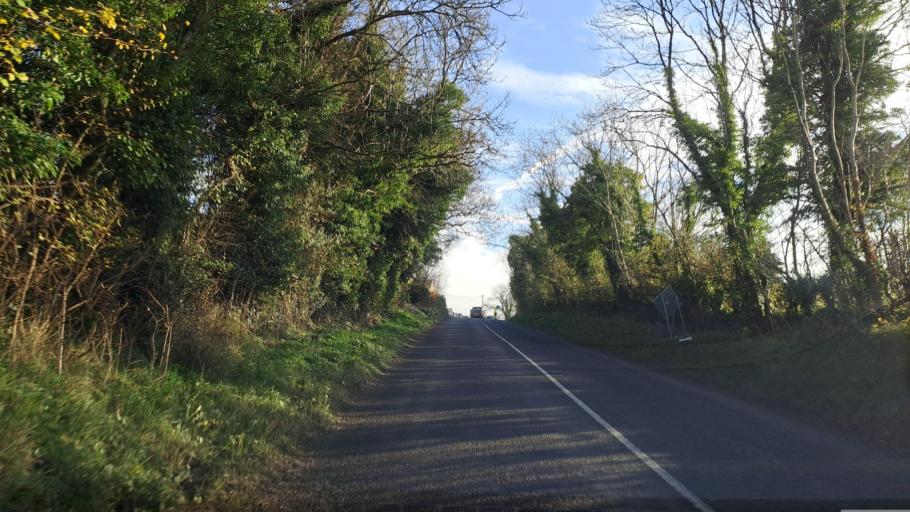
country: IE
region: Ulster
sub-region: An Cabhan
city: Kingscourt
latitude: 53.8789
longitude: -6.7245
